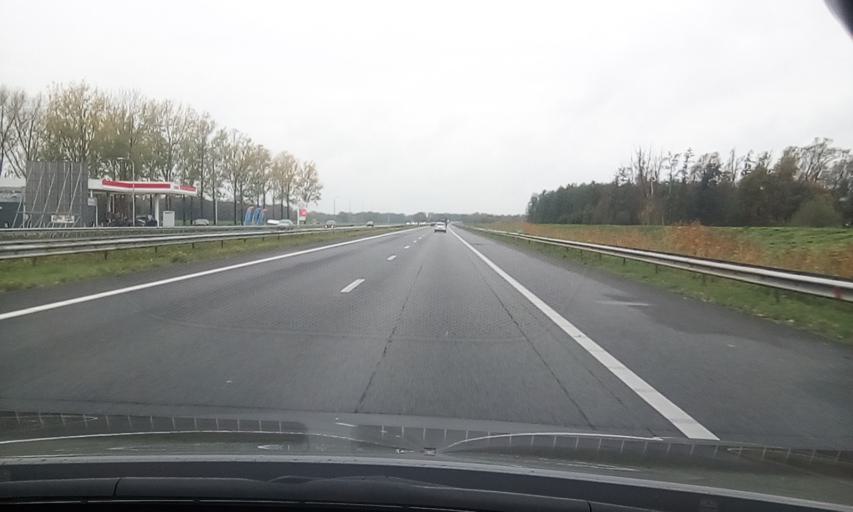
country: NL
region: Drenthe
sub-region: Gemeente De Wolden
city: Ruinen
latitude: 52.6805
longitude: 6.3595
